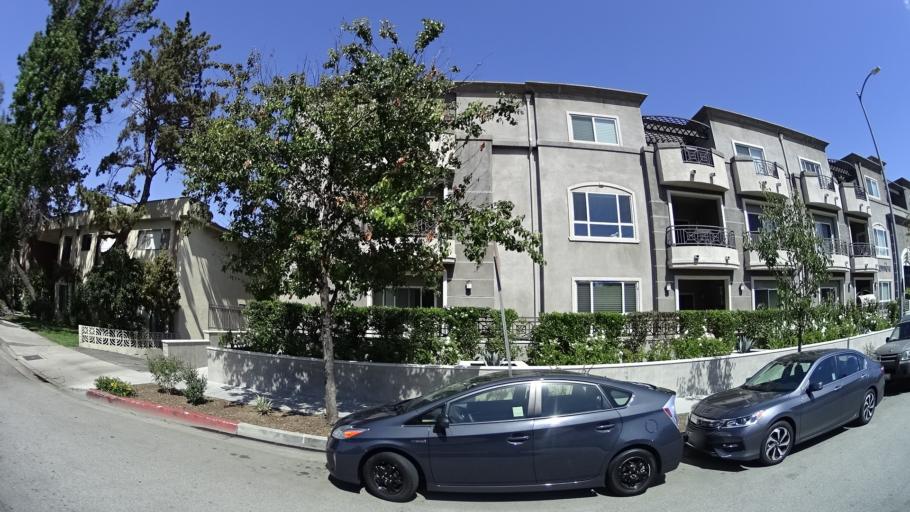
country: US
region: California
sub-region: Los Angeles County
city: North Hollywood
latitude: 34.1512
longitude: -118.4050
